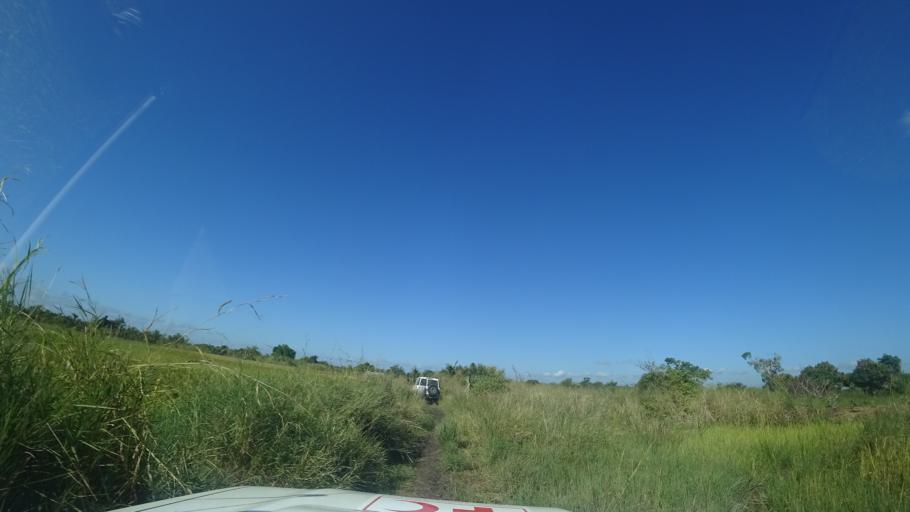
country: MZ
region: Sofala
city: Dondo
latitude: -19.3951
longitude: 34.5935
